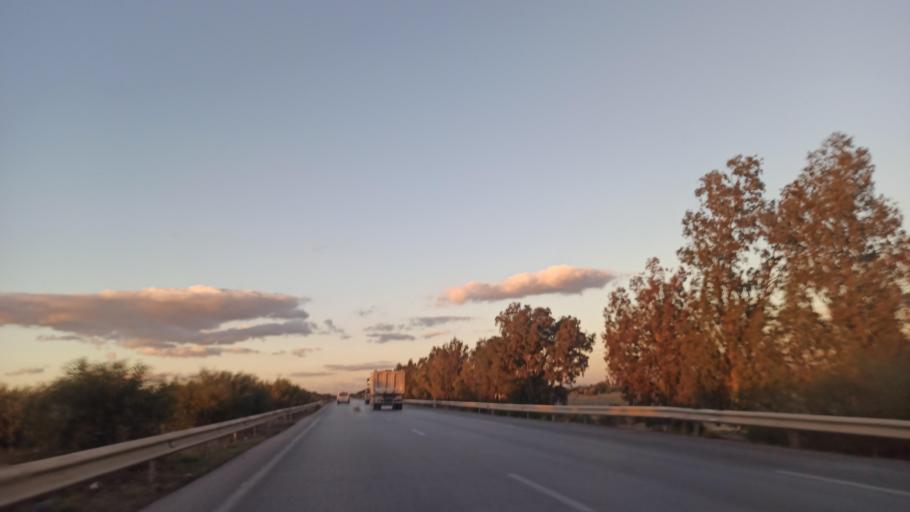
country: TN
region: Susah
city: Harqalah
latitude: 36.1315
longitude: 10.4073
